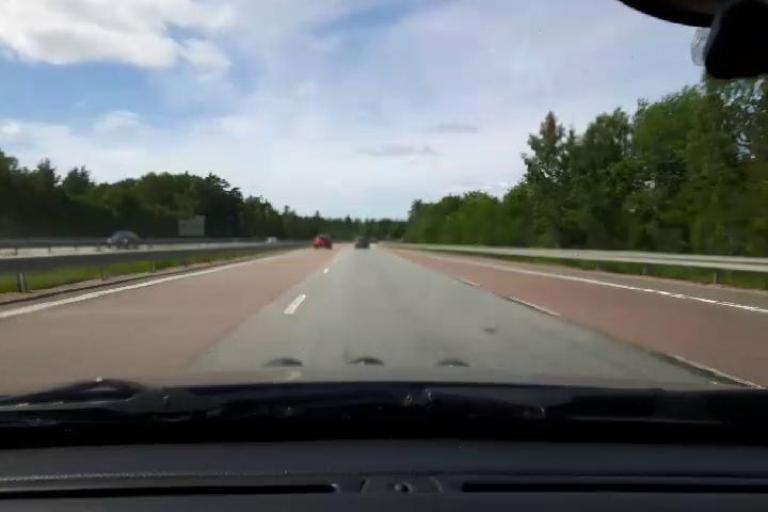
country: SE
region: Gaevleborg
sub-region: Gavle Kommun
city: Gavle
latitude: 60.6427
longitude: 17.1307
